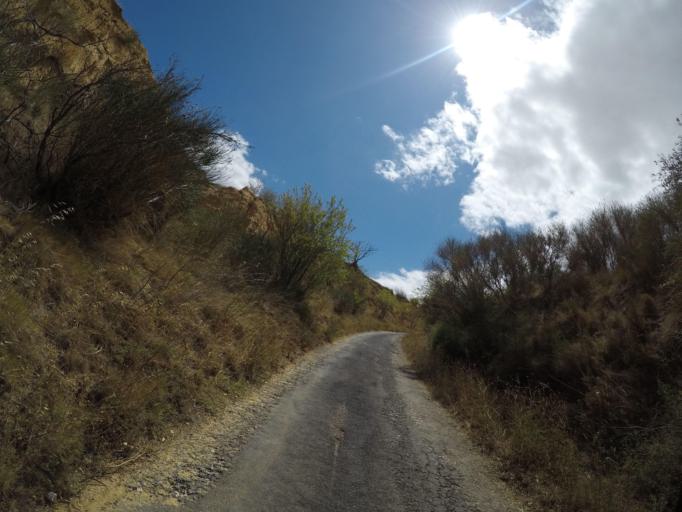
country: FR
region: Languedoc-Roussillon
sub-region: Departement des Pyrenees-Orientales
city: Baixas
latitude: 42.7435
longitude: 2.8067
